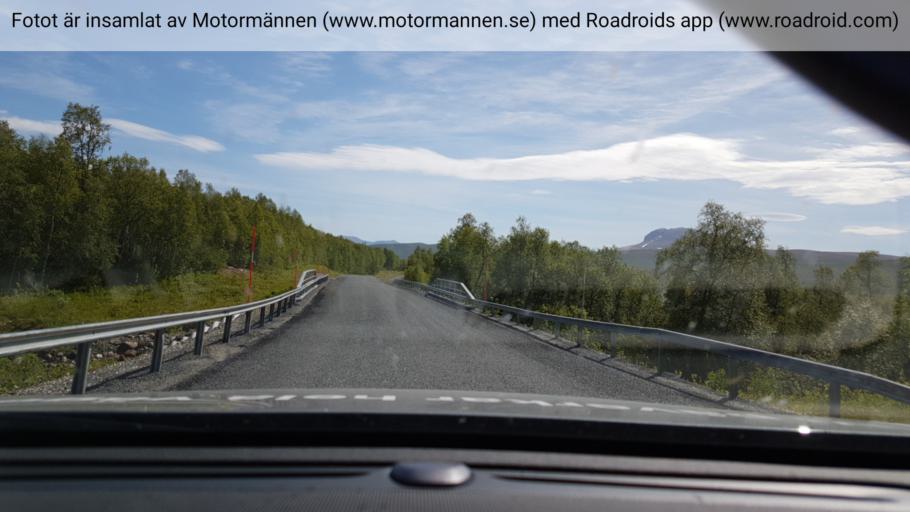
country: NO
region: Nordland
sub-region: Hattfjelldal
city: Hattfjelldal
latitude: 65.3399
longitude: 15.1027
